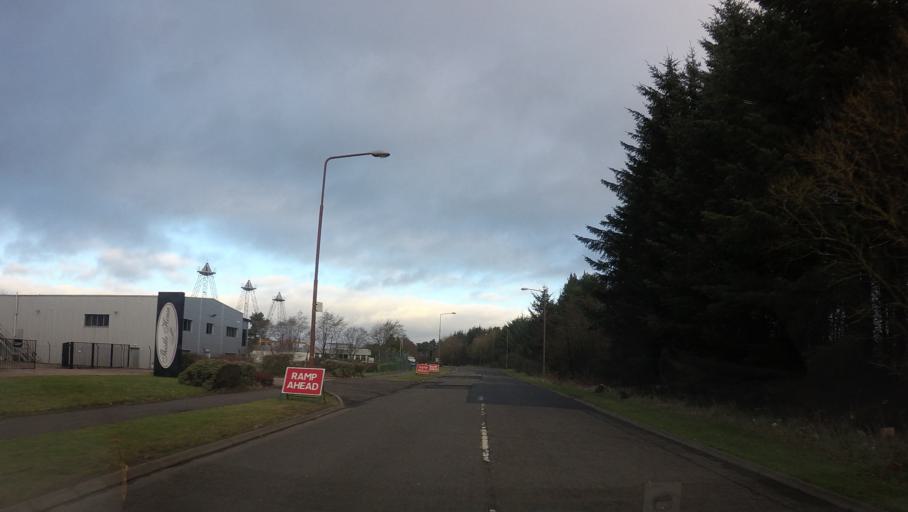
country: GB
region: Scotland
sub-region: West Lothian
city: West Calder
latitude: 55.9029
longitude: -3.5769
